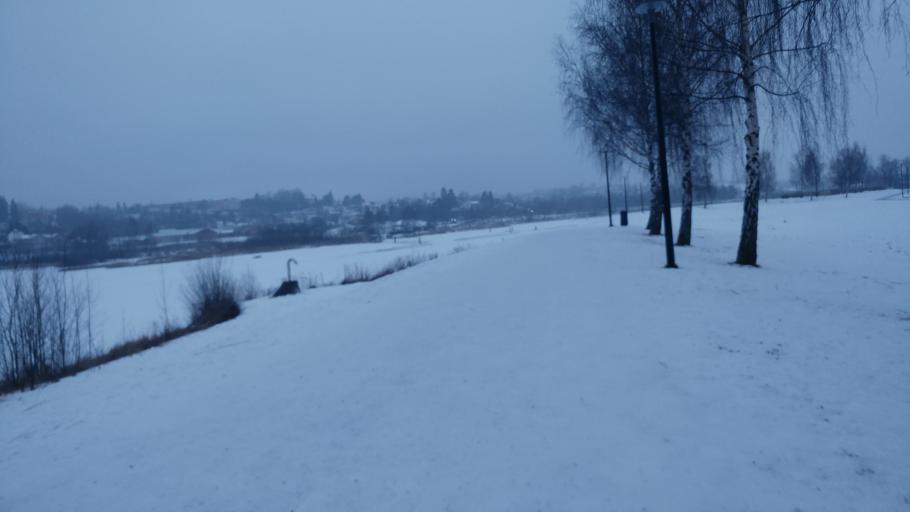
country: NO
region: Akershus
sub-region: Skedsmo
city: Lillestrom
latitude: 59.9543
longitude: 11.0351
